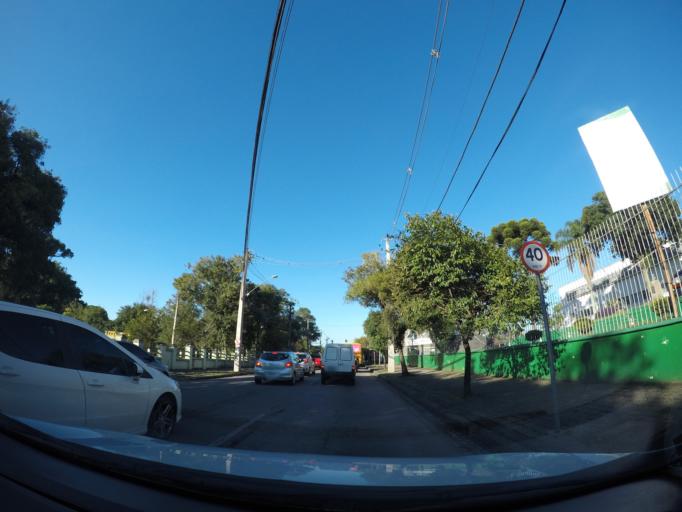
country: BR
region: Parana
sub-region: Curitiba
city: Curitiba
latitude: -25.4061
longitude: -49.2759
